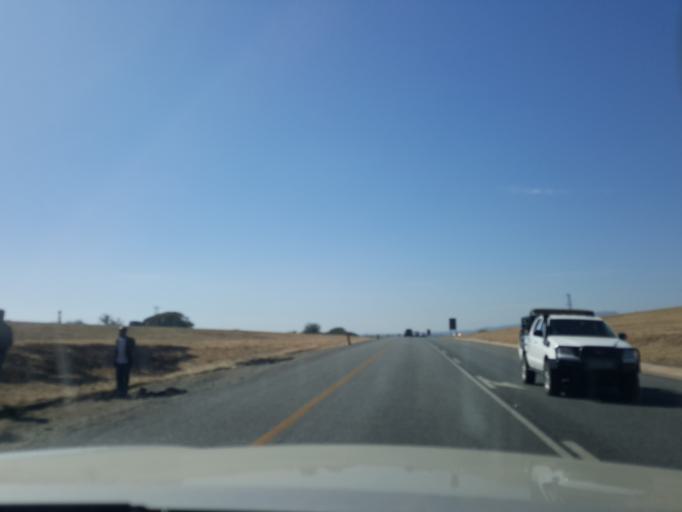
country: ZA
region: North-West
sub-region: Bojanala Platinum District Municipality
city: Brits
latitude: -25.6837
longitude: 27.7834
